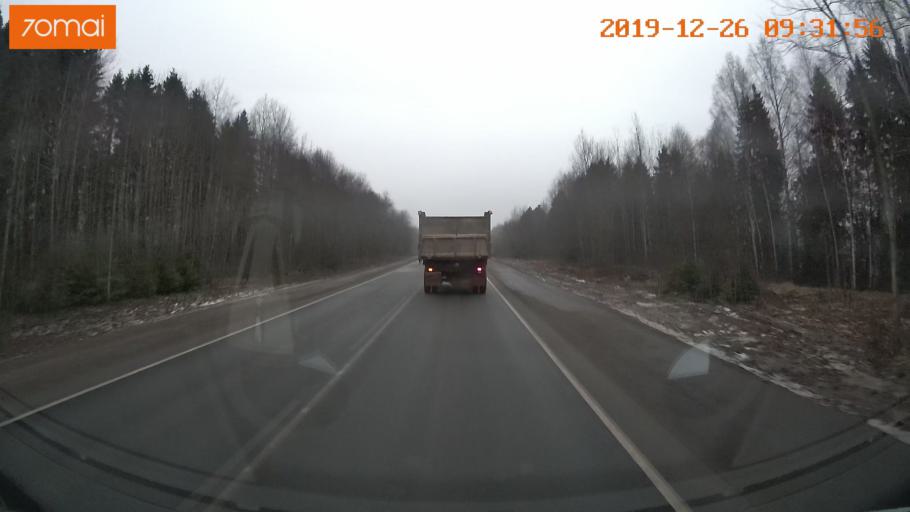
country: RU
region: Vologda
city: Gryazovets
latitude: 59.0734
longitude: 40.1223
